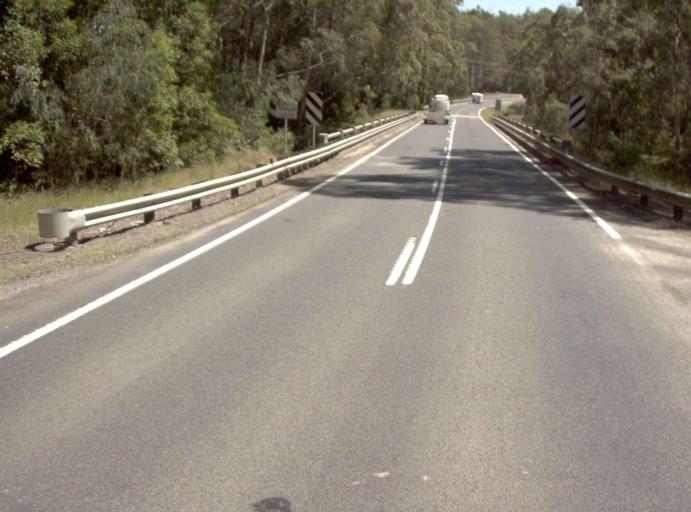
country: AU
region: New South Wales
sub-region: Bombala
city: Bombala
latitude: -37.5628
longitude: 149.0649
